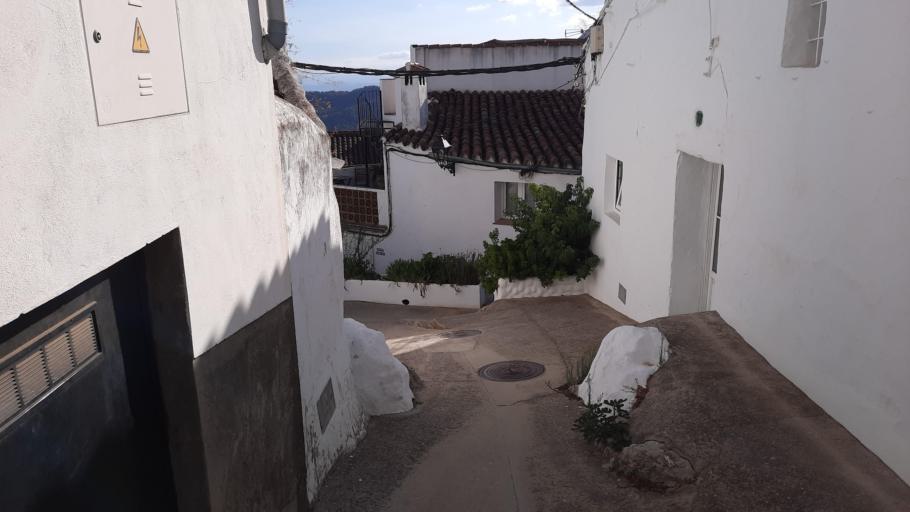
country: ES
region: Andalusia
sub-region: Provincia de Malaga
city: Gaucin
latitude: 36.5185
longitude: -5.3163
